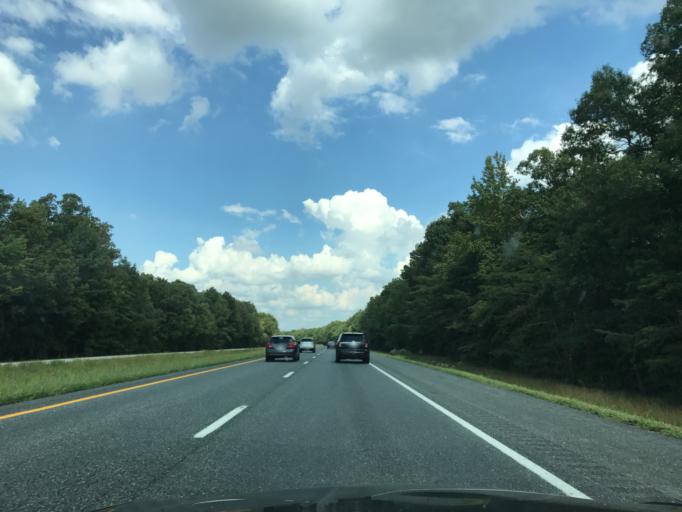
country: US
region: Maryland
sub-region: Queen Anne's County
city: Kingstown
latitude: 39.2203
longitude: -75.8793
